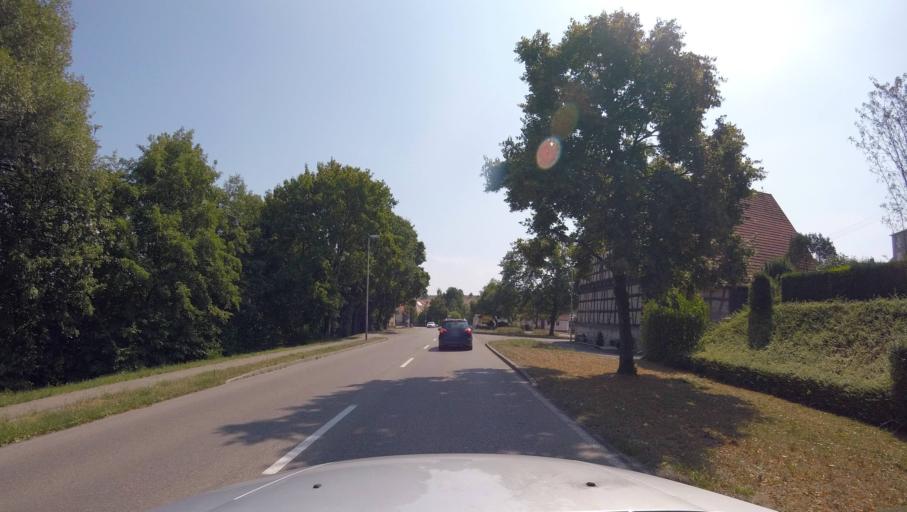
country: DE
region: Baden-Wuerttemberg
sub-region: Regierungsbezirk Stuttgart
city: Allmersbach im Tal
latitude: 48.9383
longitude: 9.4983
